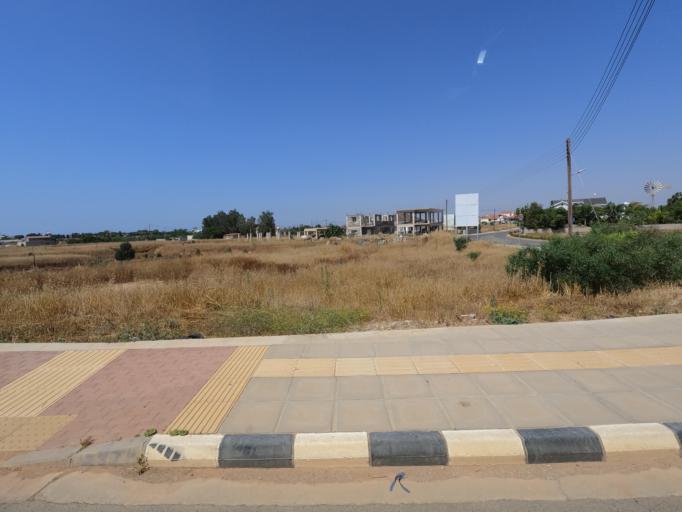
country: CY
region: Ammochostos
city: Paralimni
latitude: 35.0192
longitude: 33.9532
